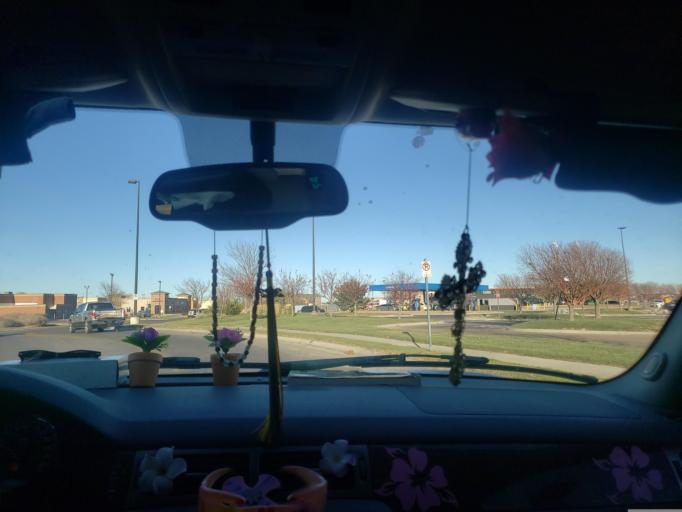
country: US
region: Kansas
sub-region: Finney County
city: Garden City
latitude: 37.9826
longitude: -100.8360
